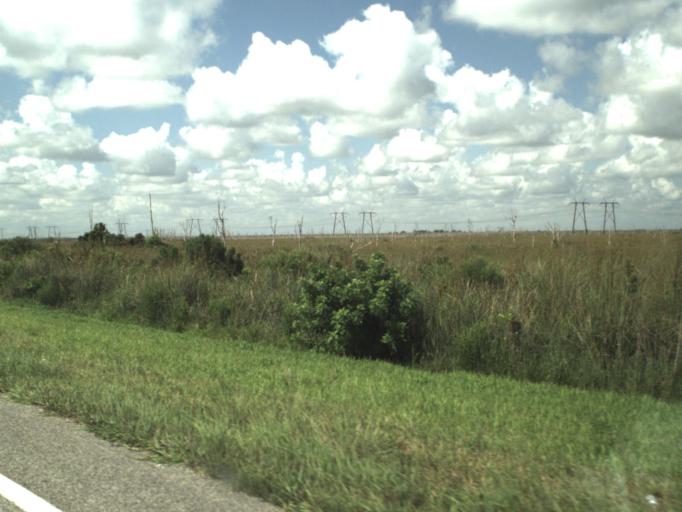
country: US
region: Florida
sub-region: Miami-Dade County
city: Palm Springs North
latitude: 25.9875
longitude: -80.4323
